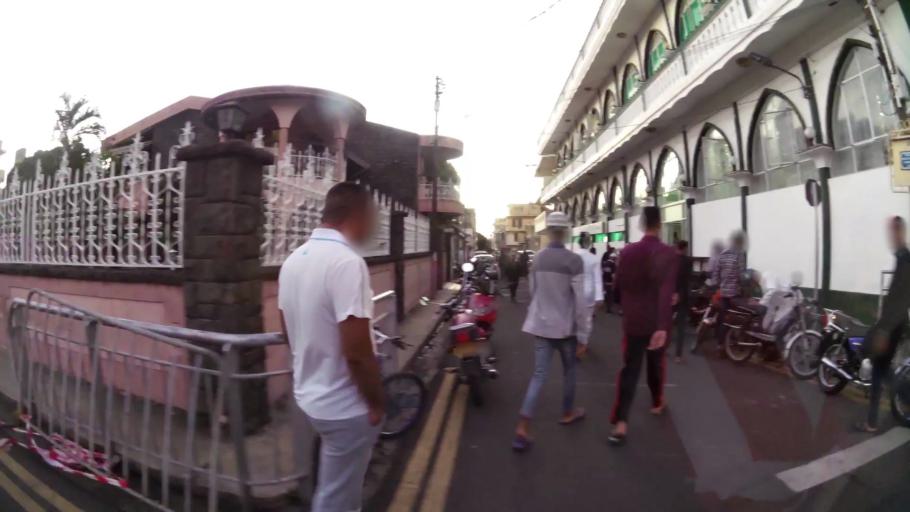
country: MU
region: Port Louis
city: Port Louis
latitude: -20.1661
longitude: 57.5171
